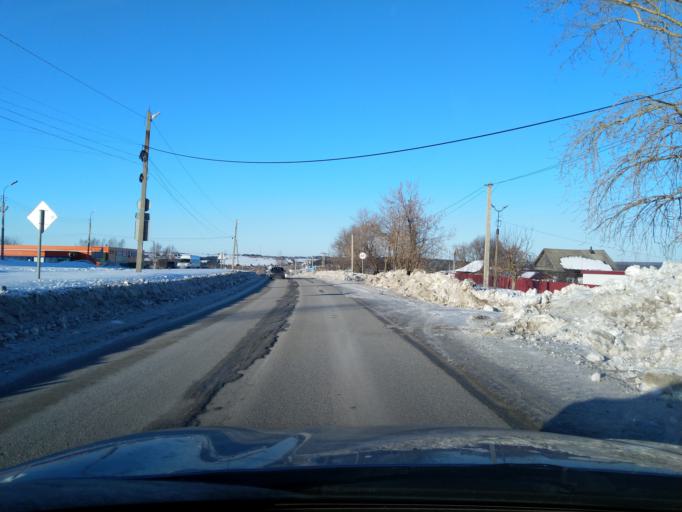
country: RU
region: Perm
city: Polazna
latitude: 58.2896
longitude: 56.4133
